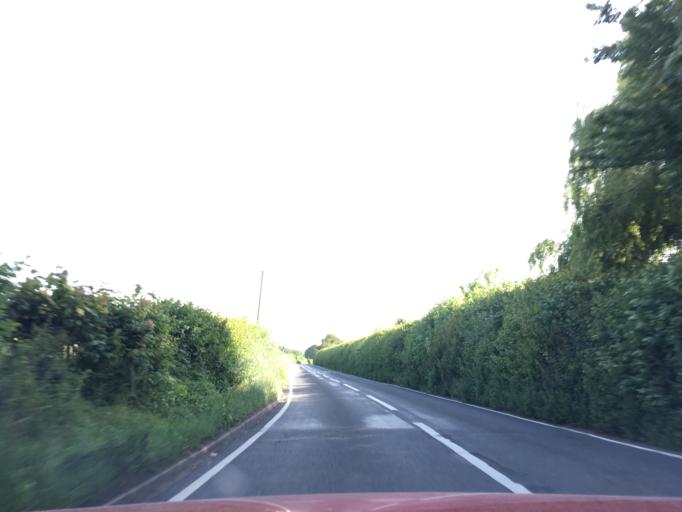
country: GB
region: England
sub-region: Oxfordshire
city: Stonesfield
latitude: 51.9262
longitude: -1.4045
